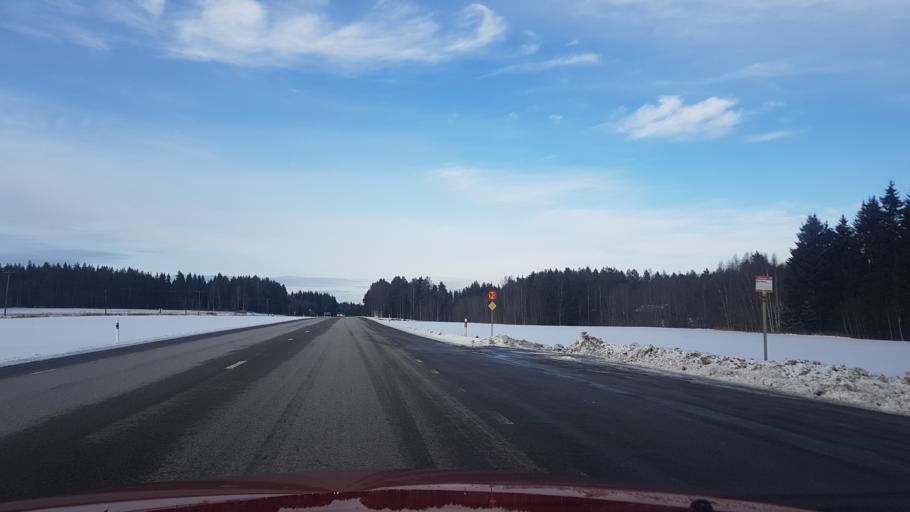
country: SE
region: Dalarna
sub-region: Leksand Municipality
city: Leksand
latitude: 60.7592
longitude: 15.0197
